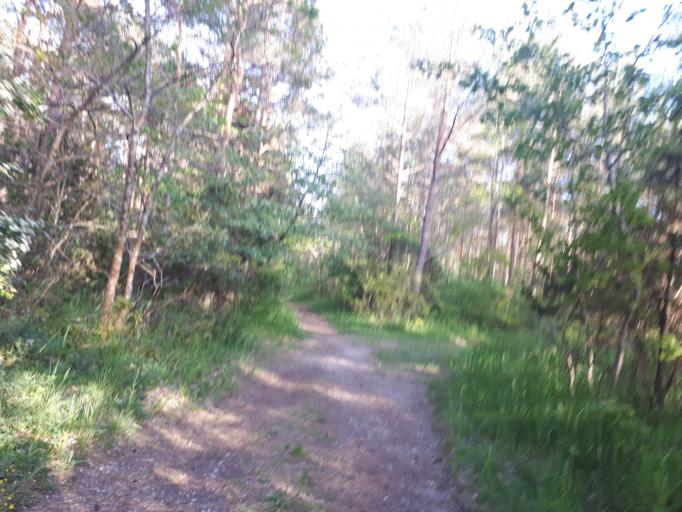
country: SE
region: Gotland
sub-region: Gotland
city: Visby
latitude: 57.6089
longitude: 18.2946
